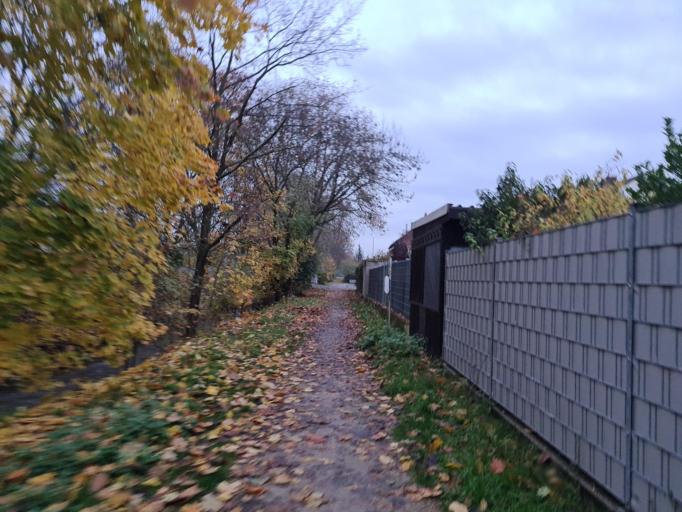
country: DE
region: Rheinland-Pfalz
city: Kleinniedesheim
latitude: 49.6085
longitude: 8.2967
